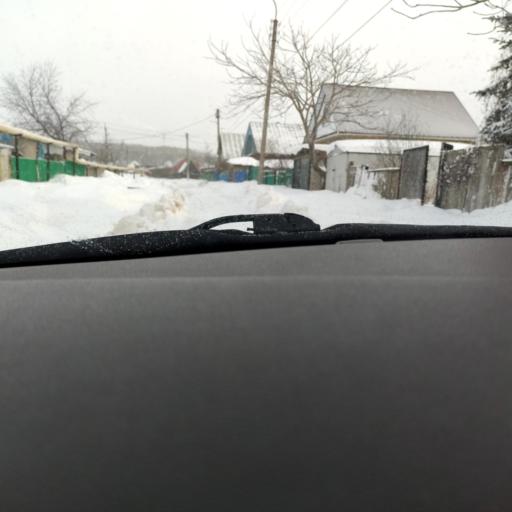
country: RU
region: Bashkortostan
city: Blagoveshchensk
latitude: 55.0267
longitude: 56.0024
